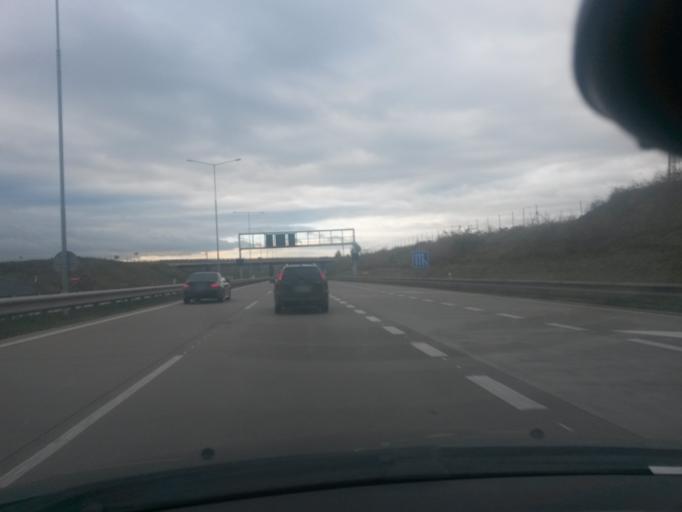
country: CZ
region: Central Bohemia
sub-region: Okres Praha-Zapad
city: Pruhonice
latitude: 49.9763
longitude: 14.5900
